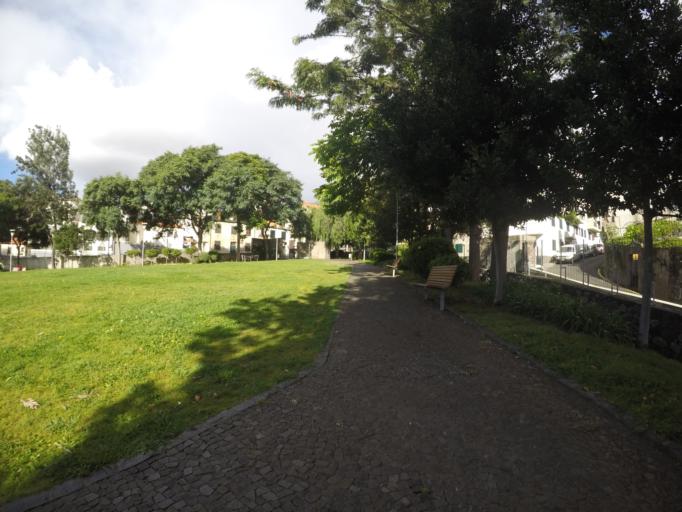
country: PT
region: Madeira
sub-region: Funchal
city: Nossa Senhora do Monte
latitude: 32.6544
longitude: -16.9118
